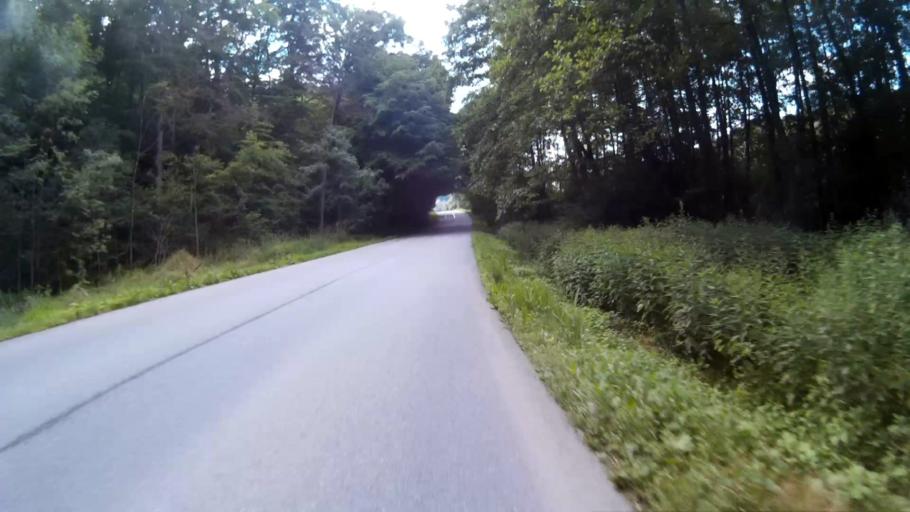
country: CZ
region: South Moravian
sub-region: Okres Brno-Venkov
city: Rosice
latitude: 49.1634
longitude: 16.4311
